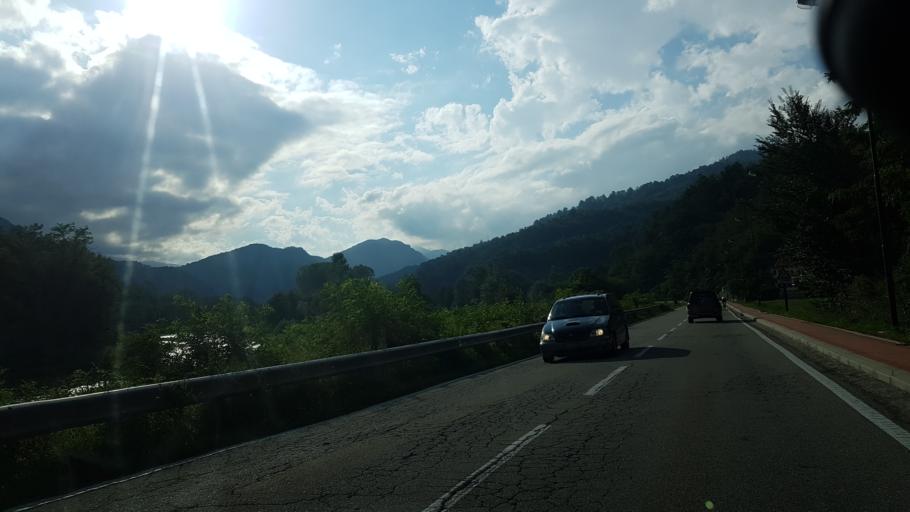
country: IT
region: Piedmont
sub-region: Provincia di Cuneo
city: Venasca
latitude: 44.5667
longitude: 7.3925
